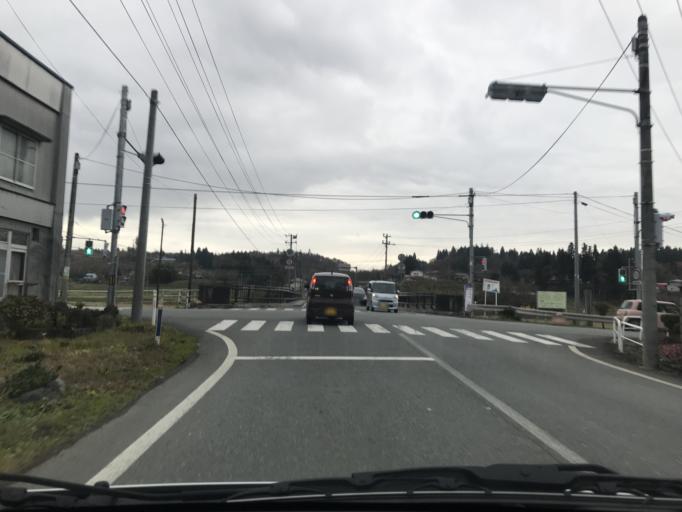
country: JP
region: Iwate
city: Ichinoseki
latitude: 39.0213
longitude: 141.3305
